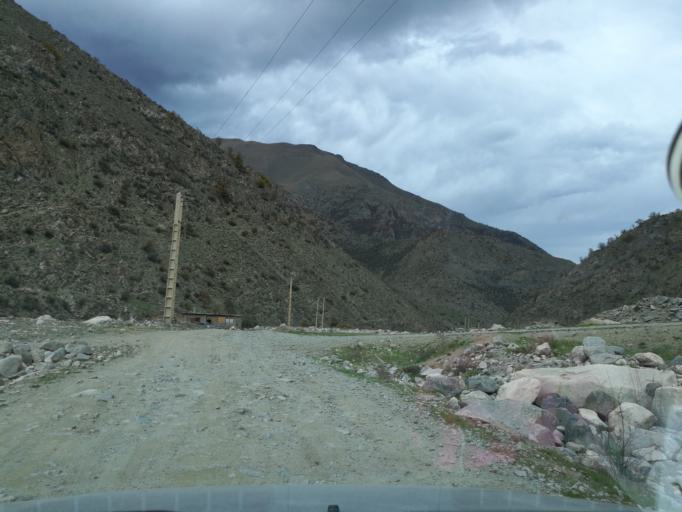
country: IR
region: Mazandaran
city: `Abbasabad
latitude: 36.4310
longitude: 51.0419
